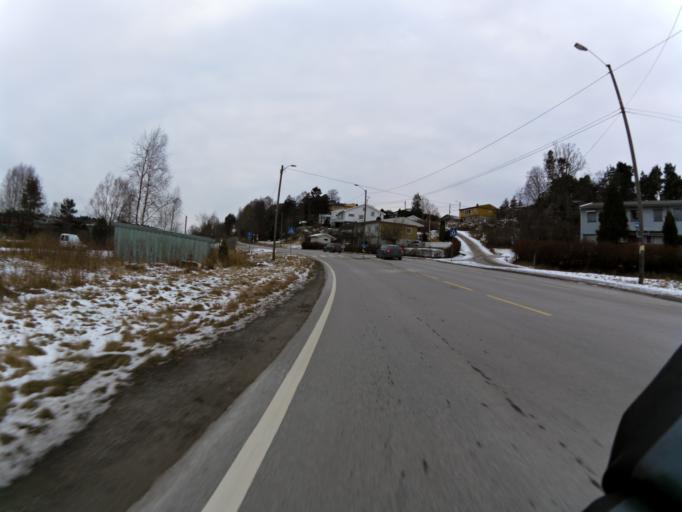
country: NO
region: Ostfold
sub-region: Fredrikstad
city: Fredrikstad
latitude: 59.2282
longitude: 10.9005
